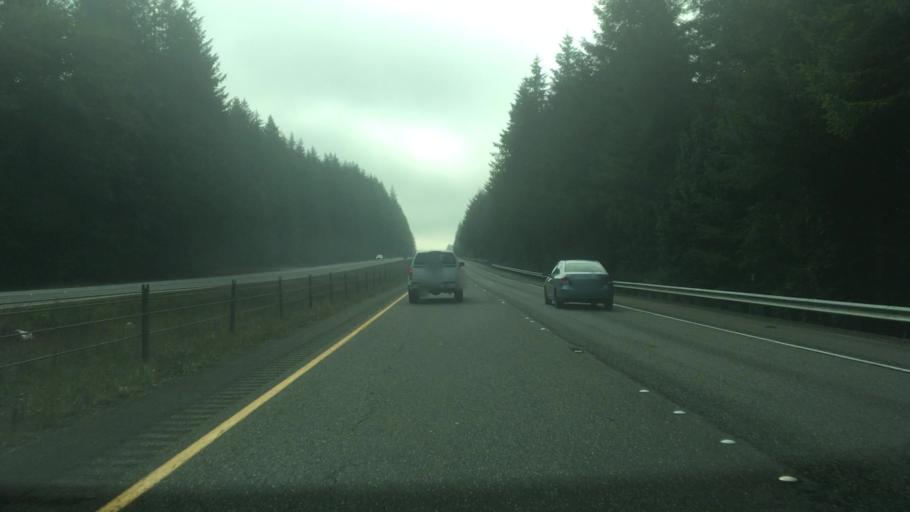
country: US
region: Washington
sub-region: Grays Harbor County
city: McCleary
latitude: 47.0357
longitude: -123.3350
